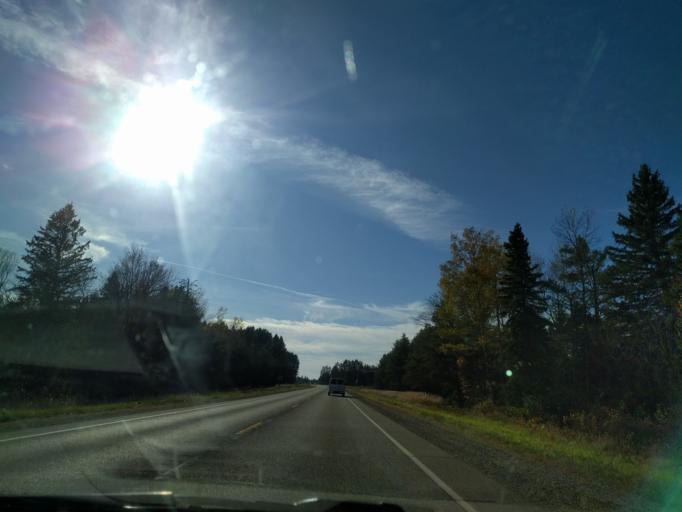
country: US
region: Wisconsin
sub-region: Marinette County
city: Niagara
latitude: 45.6412
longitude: -87.9763
